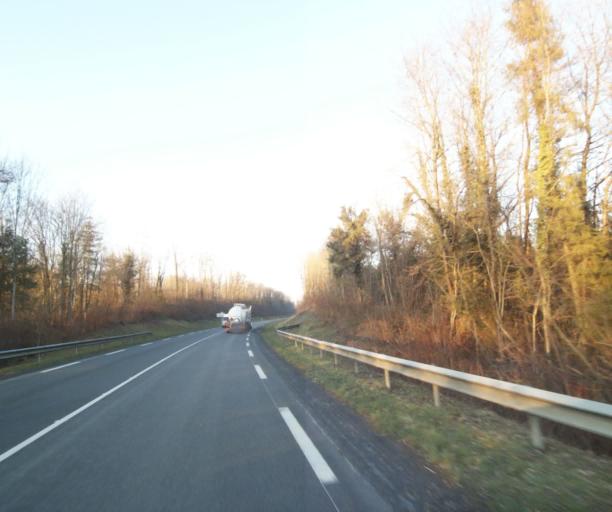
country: FR
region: Champagne-Ardenne
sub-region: Departement de la Haute-Marne
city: Bienville
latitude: 48.5670
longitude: 5.0352
